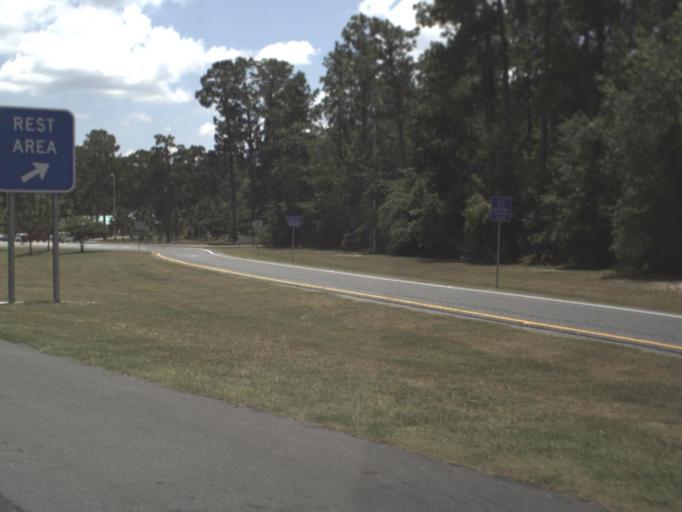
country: US
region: Florida
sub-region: Madison County
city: Madison
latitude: 30.3690
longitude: -83.2513
